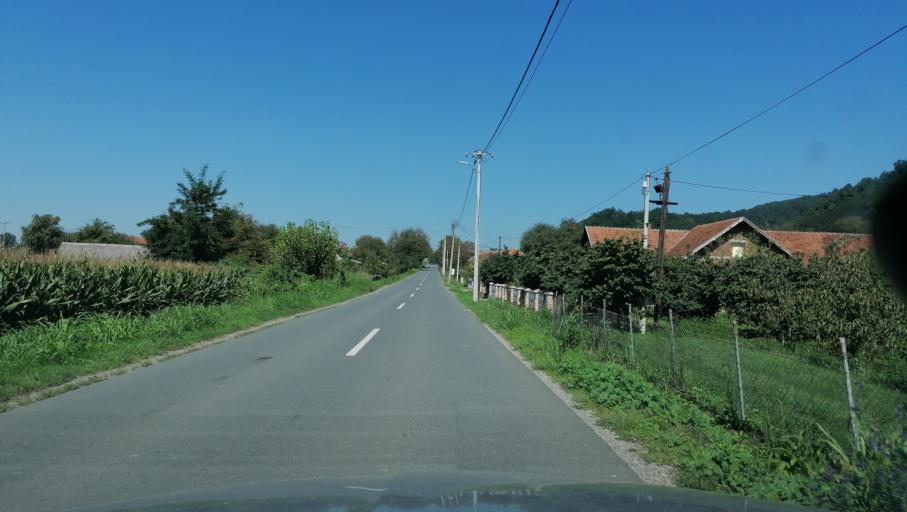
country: RS
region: Central Serbia
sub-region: Raski Okrug
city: Vrnjacka Banja
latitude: 43.6722
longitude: 20.9046
